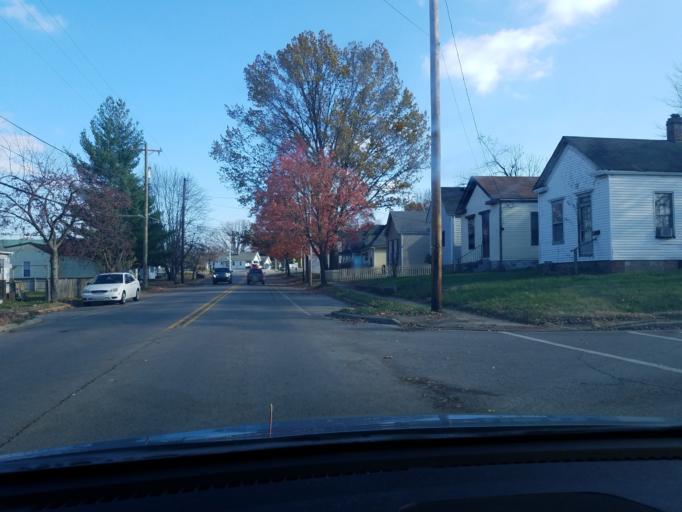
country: US
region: Indiana
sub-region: Floyd County
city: New Albany
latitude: 38.3049
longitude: -85.8146
